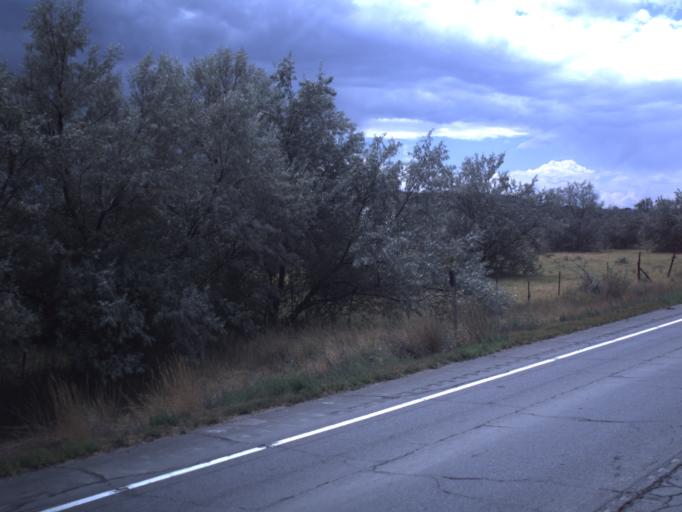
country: US
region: Utah
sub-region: Duchesne County
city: Roosevelt
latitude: 40.1811
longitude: -110.1094
